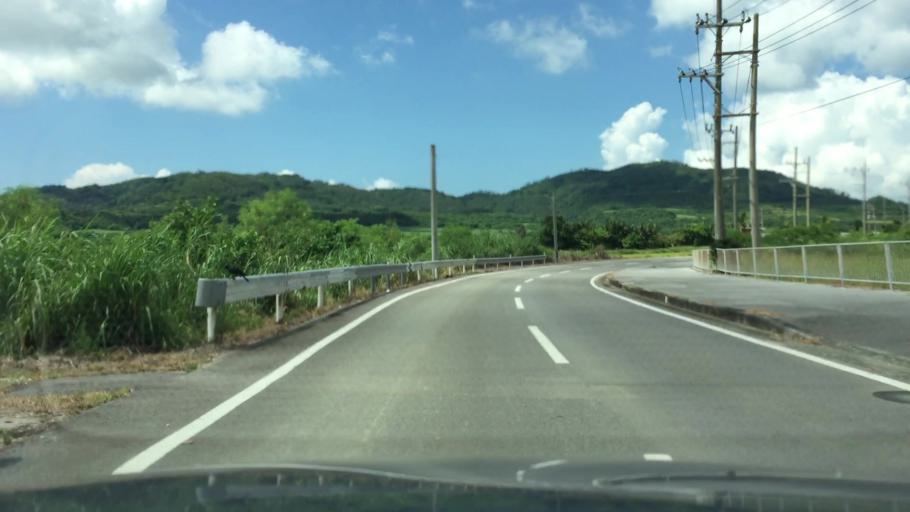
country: JP
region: Okinawa
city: Ishigaki
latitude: 24.3908
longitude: 124.1507
